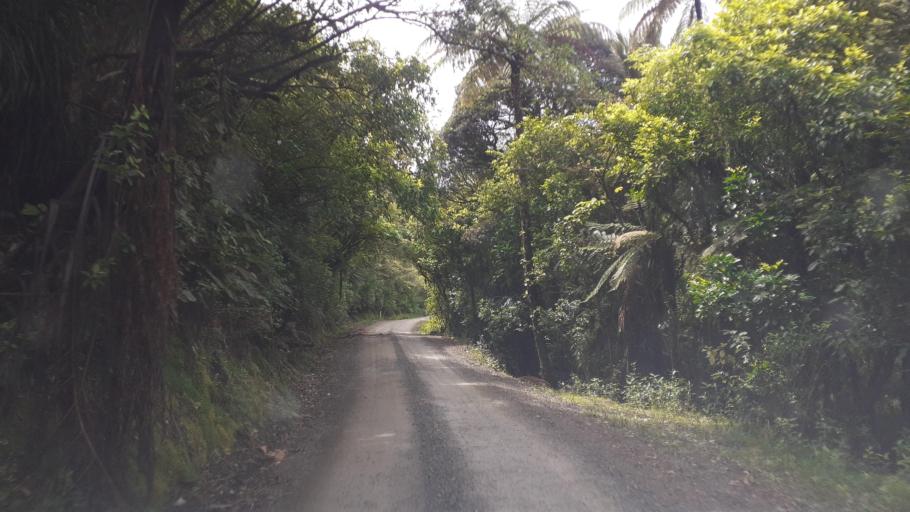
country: NZ
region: Northland
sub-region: Far North District
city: Waimate North
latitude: -35.5730
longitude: 173.5621
